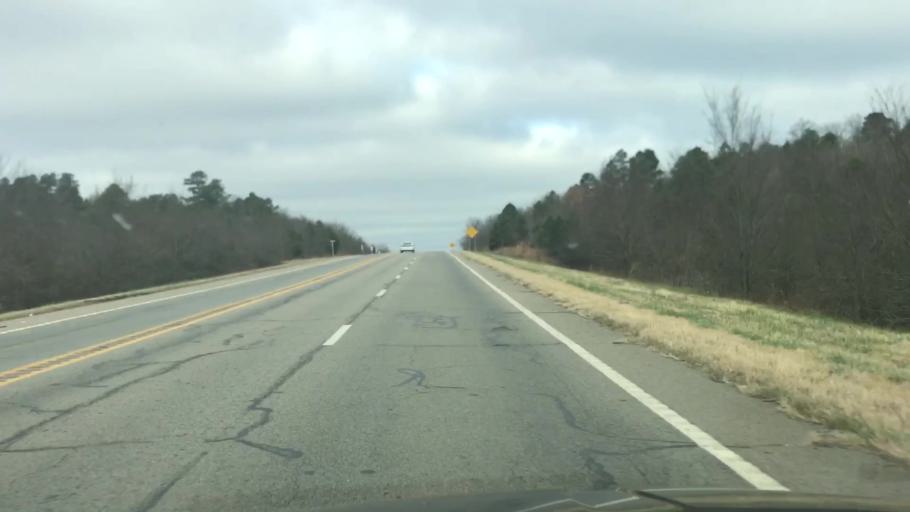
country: US
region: Arkansas
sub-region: Scott County
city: Waldron
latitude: 34.8603
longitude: -94.0705
